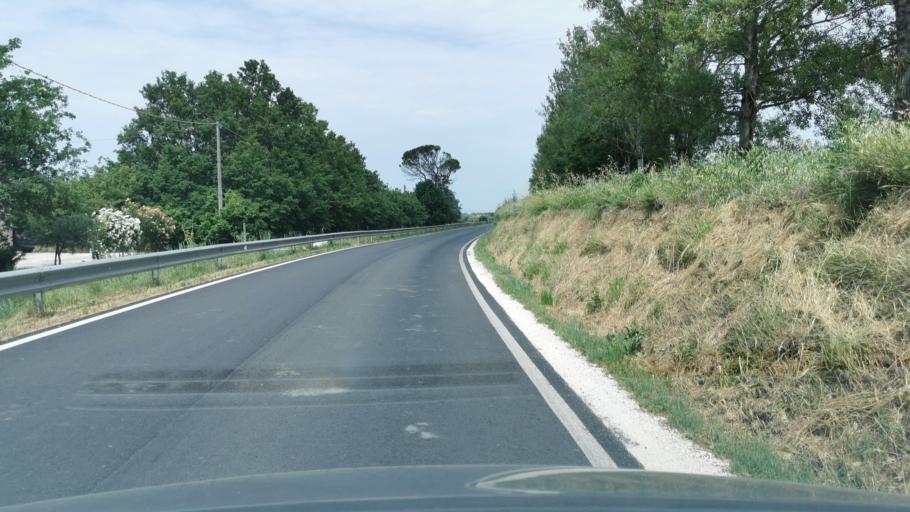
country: IT
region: Emilia-Romagna
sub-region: Provincia di Ravenna
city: Villanova
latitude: 44.4735
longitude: 12.0294
